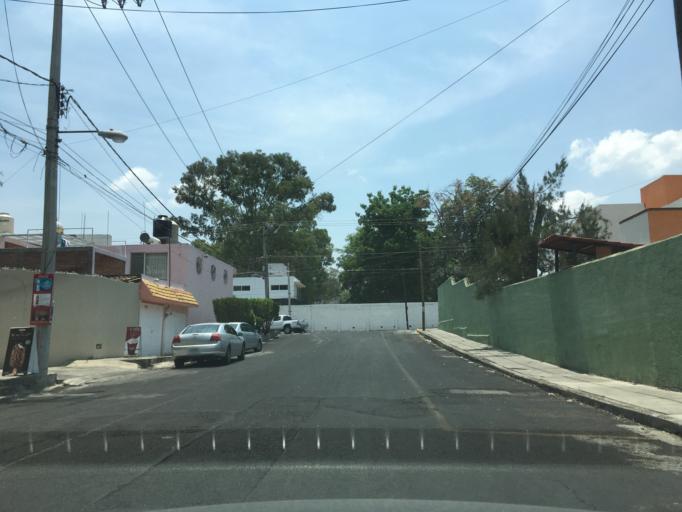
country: MX
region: Michoacan
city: Morelia
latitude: 19.7011
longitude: -101.1697
